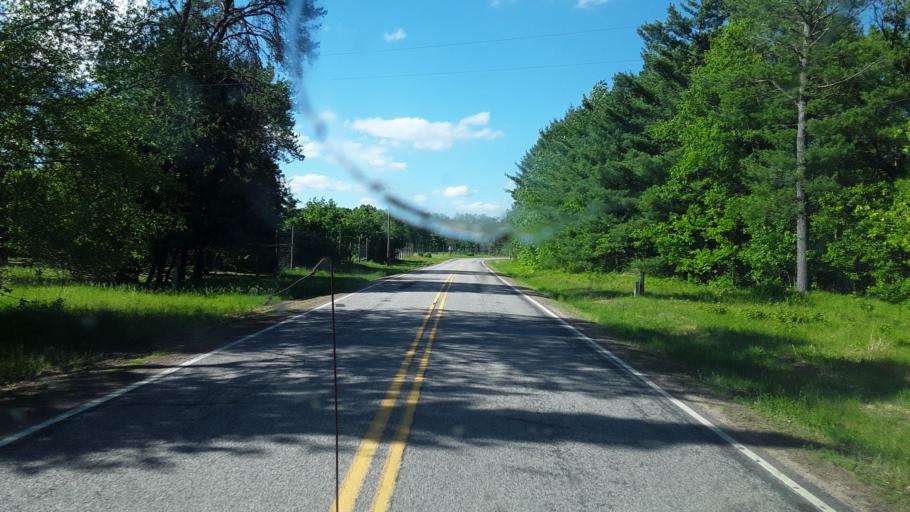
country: US
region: Wisconsin
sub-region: Wood County
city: Nekoosa
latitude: 44.3076
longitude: -90.1297
